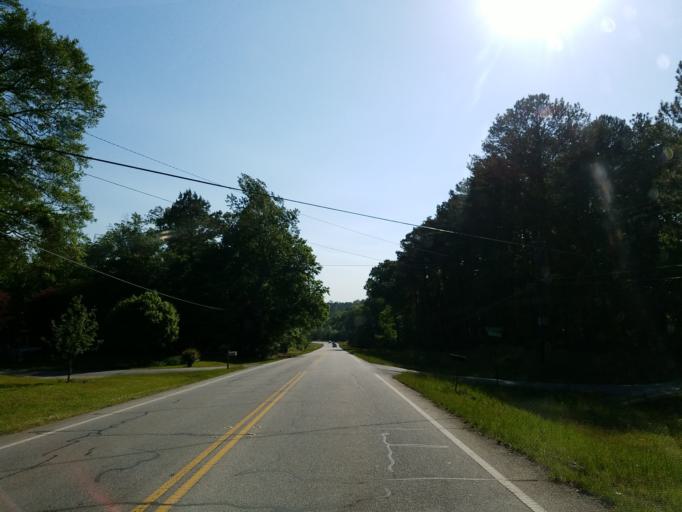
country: US
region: Georgia
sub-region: Paulding County
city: Dallas
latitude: 33.9094
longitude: -84.8679
